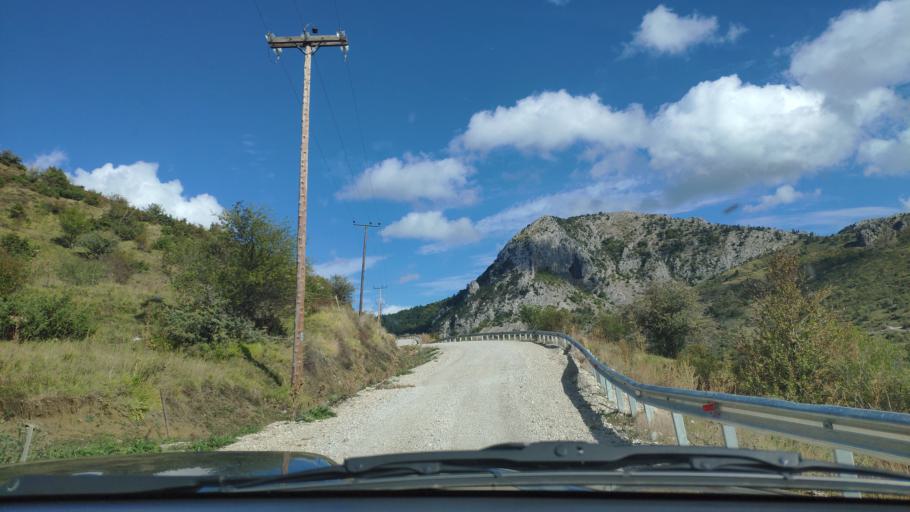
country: AL
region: Korce
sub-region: Rrethi i Devollit
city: Miras
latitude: 40.3968
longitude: 20.8373
